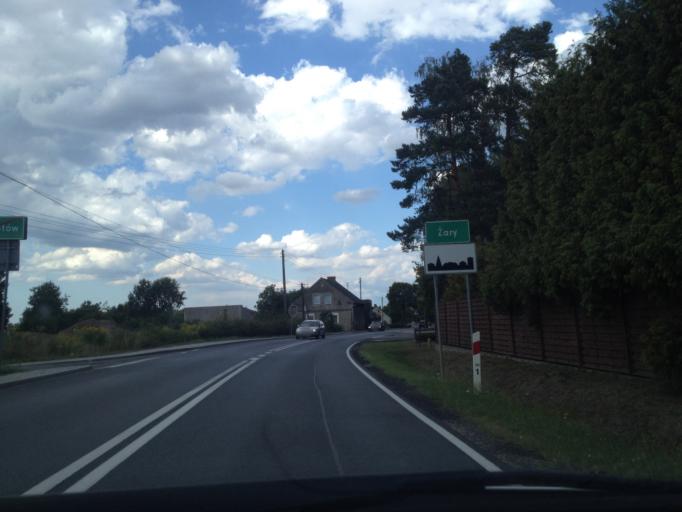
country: PL
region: Lubusz
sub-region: Powiat zarski
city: Zary
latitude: 51.6135
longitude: 15.1058
